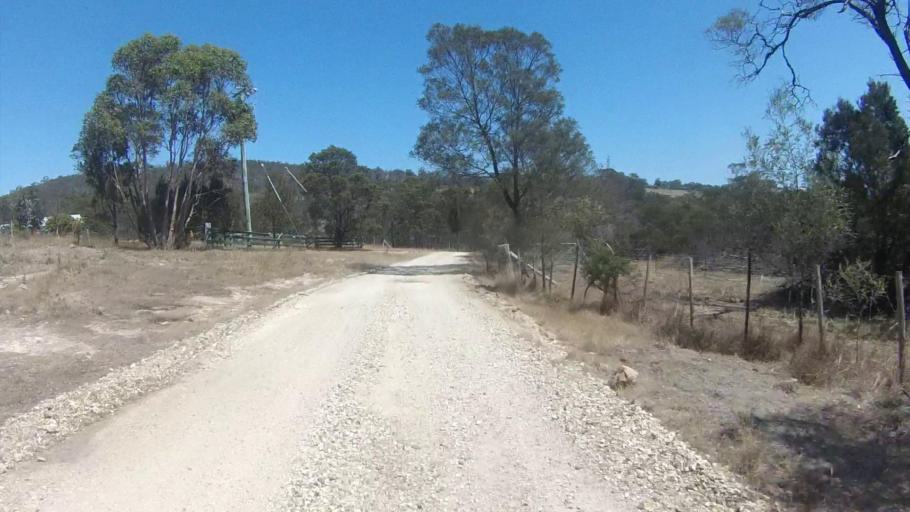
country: AU
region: Tasmania
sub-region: Sorell
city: Sorell
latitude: -42.8256
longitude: 147.6616
